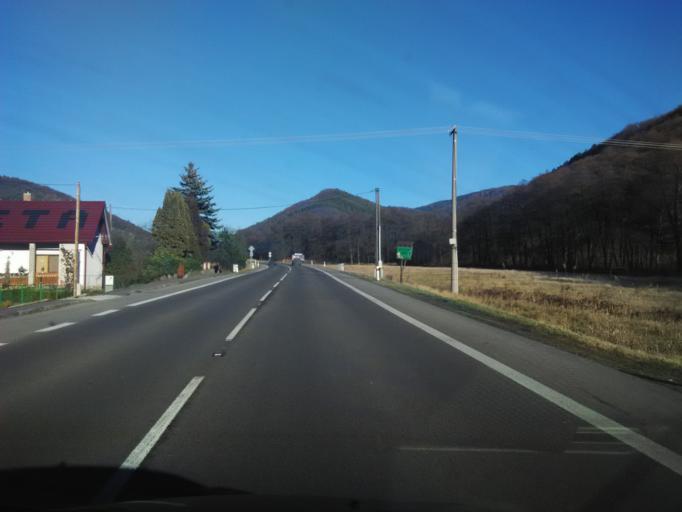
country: SK
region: Banskobystricky
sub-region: Okres Ziar nad Hronom
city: Kremnica
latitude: 48.6573
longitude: 18.9105
